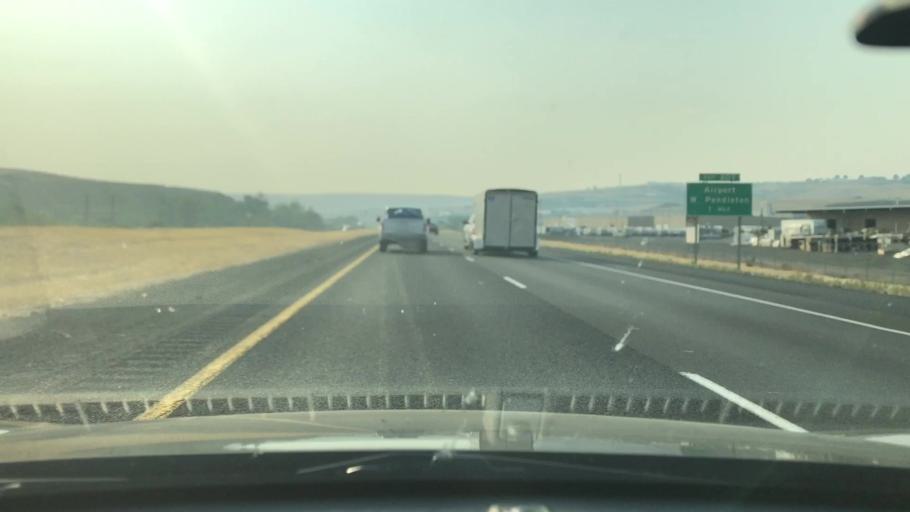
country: US
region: Oregon
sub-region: Umatilla County
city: Pendleton
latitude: 45.6672
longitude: -118.8185
